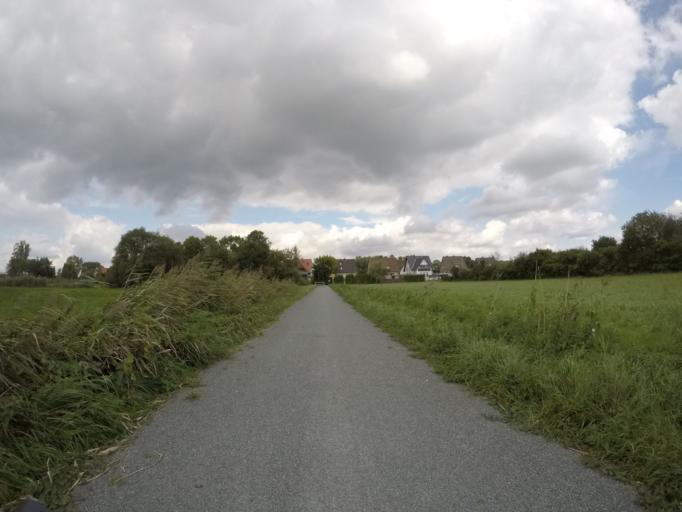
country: DE
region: North Rhine-Westphalia
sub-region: Regierungsbezirk Detmold
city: Herford
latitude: 52.1350
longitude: 8.6444
